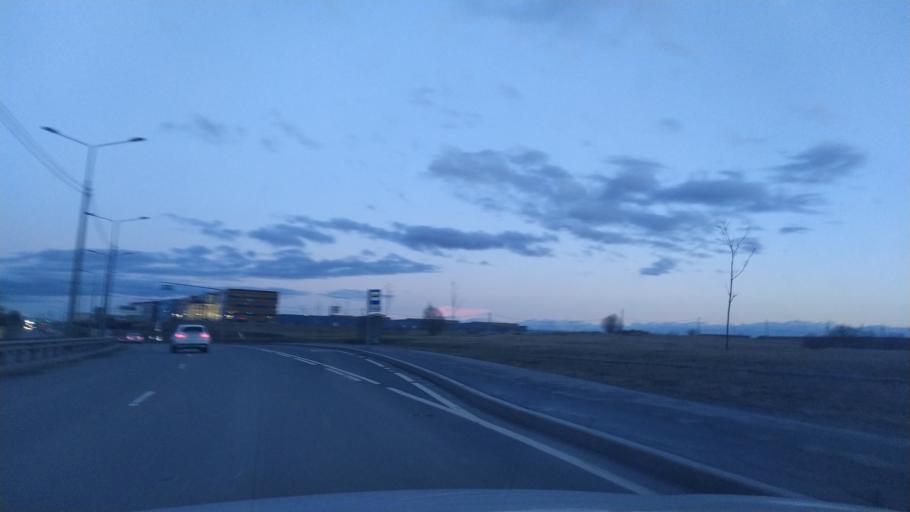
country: RU
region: St.-Petersburg
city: Aleksandrovskaya
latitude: 59.7690
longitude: 30.3457
